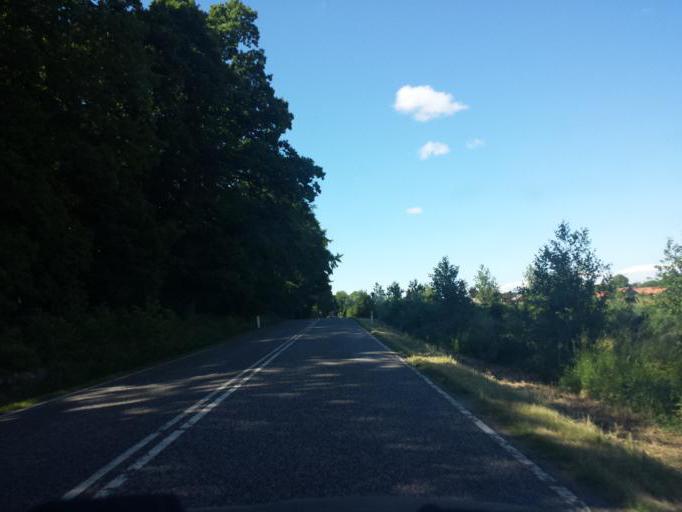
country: DK
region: Capital Region
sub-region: Egedal Kommune
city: Ganlose
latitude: 55.8095
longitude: 12.2617
